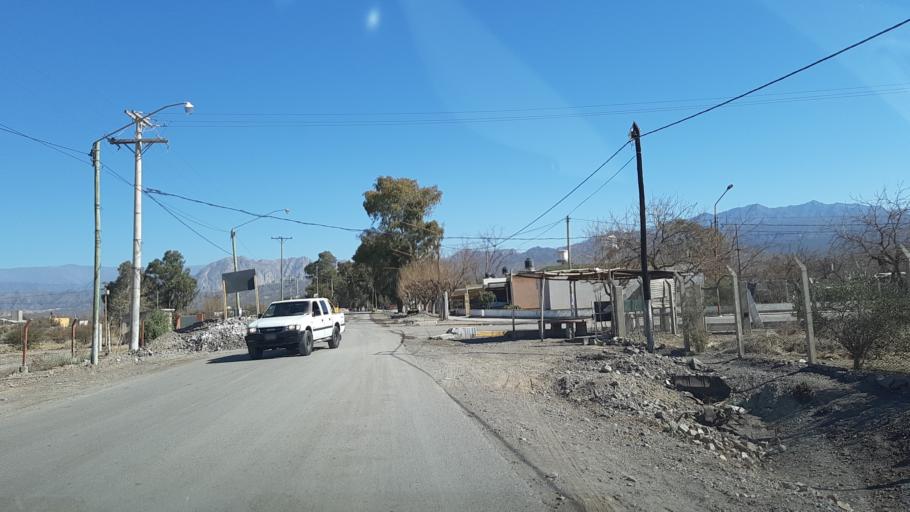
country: AR
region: San Juan
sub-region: Departamento de Zonda
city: Zonda
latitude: -31.4693
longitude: -68.7326
